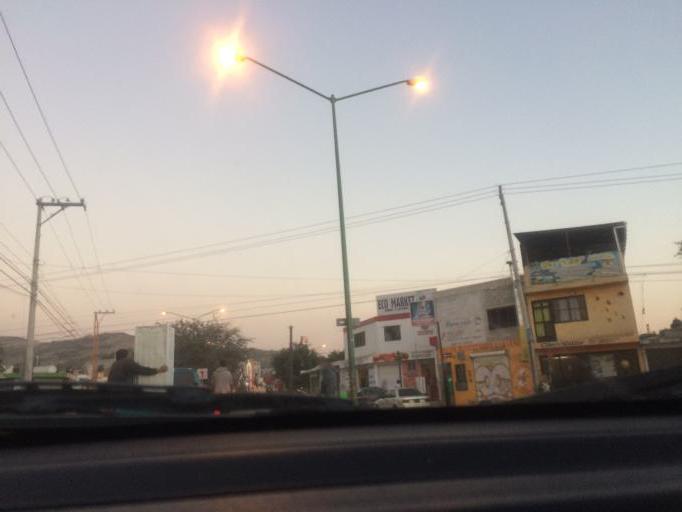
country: MX
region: Guanajuato
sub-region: Leon
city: Fraccionamiento Paraiso Real
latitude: 21.1182
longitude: -101.5881
